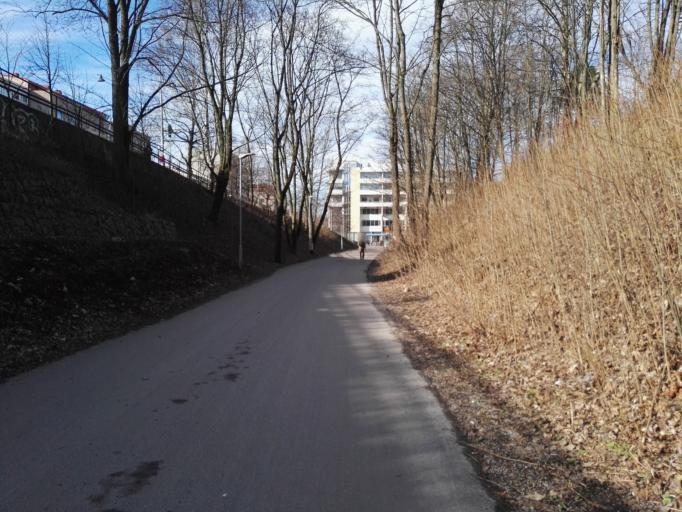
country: FI
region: Paijanne Tavastia
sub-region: Lahti
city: Lahti
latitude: 60.9804
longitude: 25.6610
